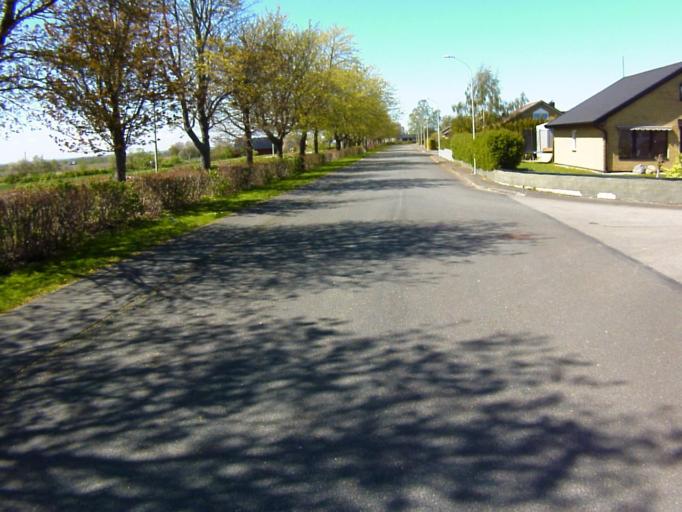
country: SE
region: Skane
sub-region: Kristianstads Kommun
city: Kristianstad
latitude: 56.0483
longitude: 14.2151
